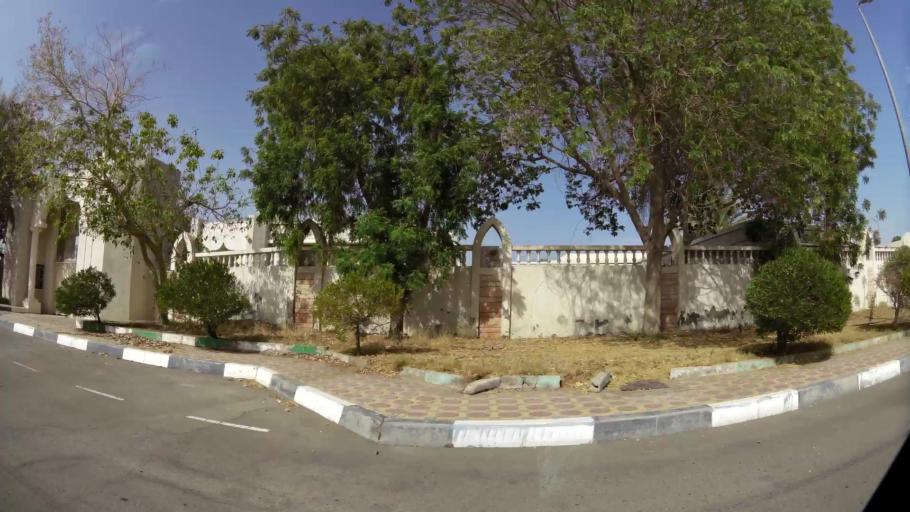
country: AE
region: Abu Dhabi
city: Al Ain
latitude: 24.2394
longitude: 55.6795
